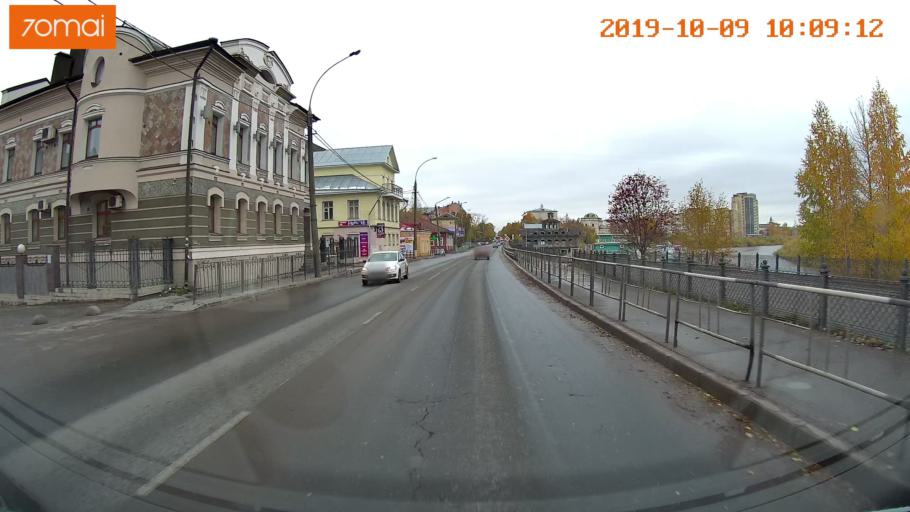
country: RU
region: Vologda
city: Vologda
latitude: 59.2104
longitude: 39.9063
